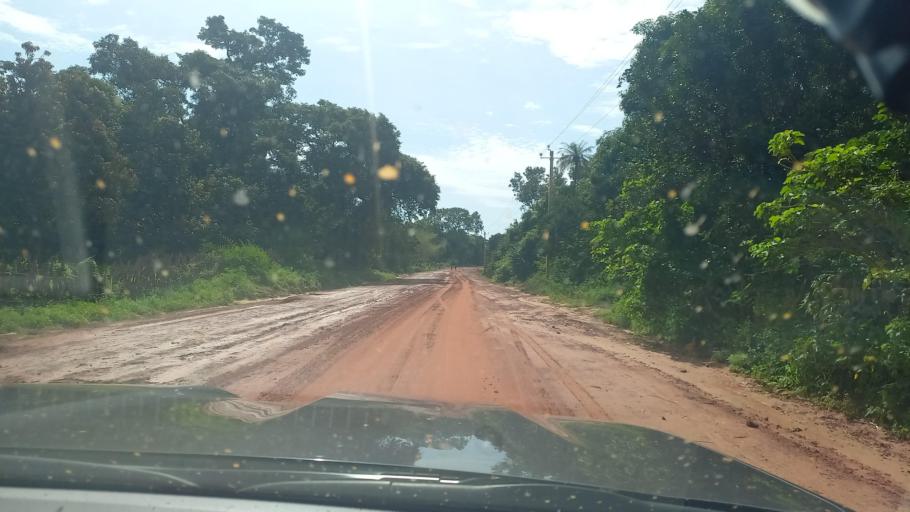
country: SN
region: Ziguinchor
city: Ziguinchor
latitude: 12.6738
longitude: -16.1926
